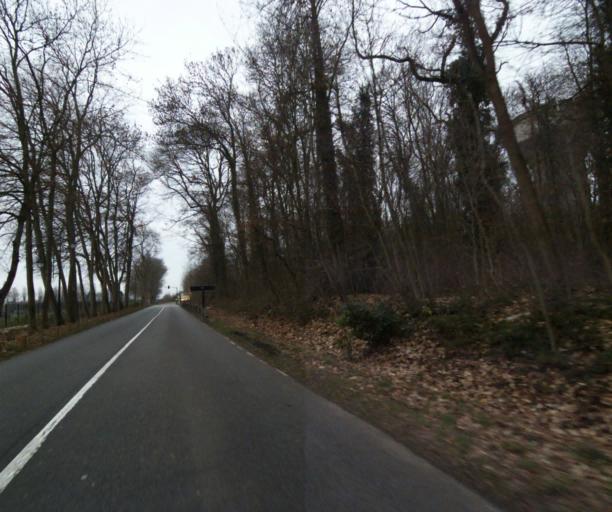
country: FR
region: Ile-de-France
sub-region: Departement des Hauts-de-Seine
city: Vaucresson
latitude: 48.8354
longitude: 2.1461
